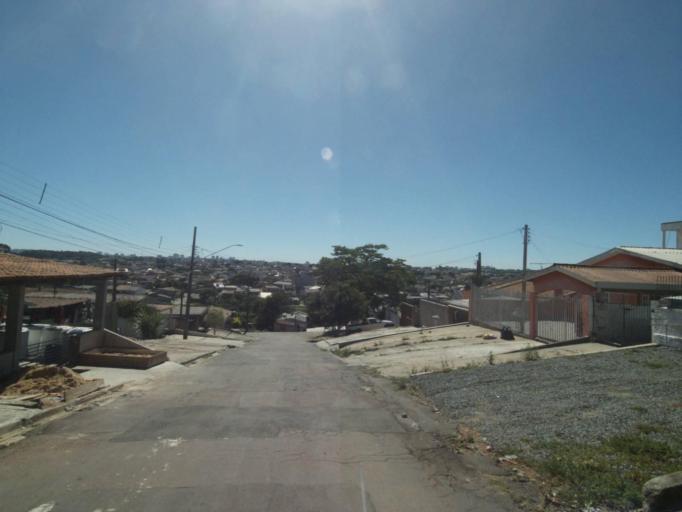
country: BR
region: Parana
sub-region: Curitiba
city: Curitiba
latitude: -25.4863
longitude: -49.3392
